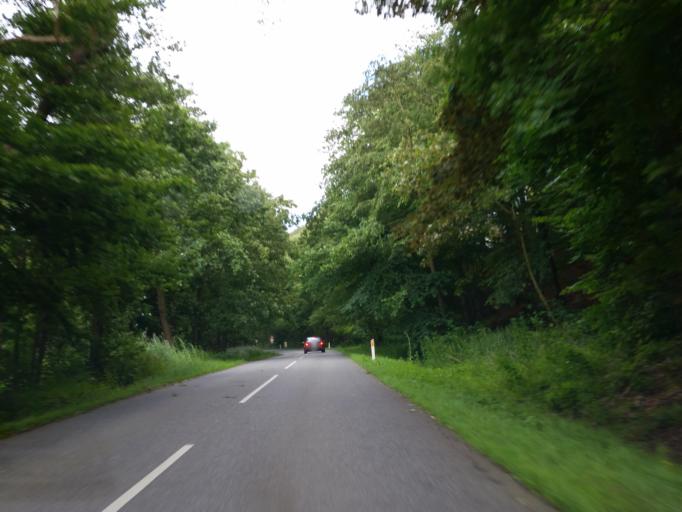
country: DK
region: South Denmark
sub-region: Vejle Kommune
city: Borkop
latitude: 55.6924
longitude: 9.6111
